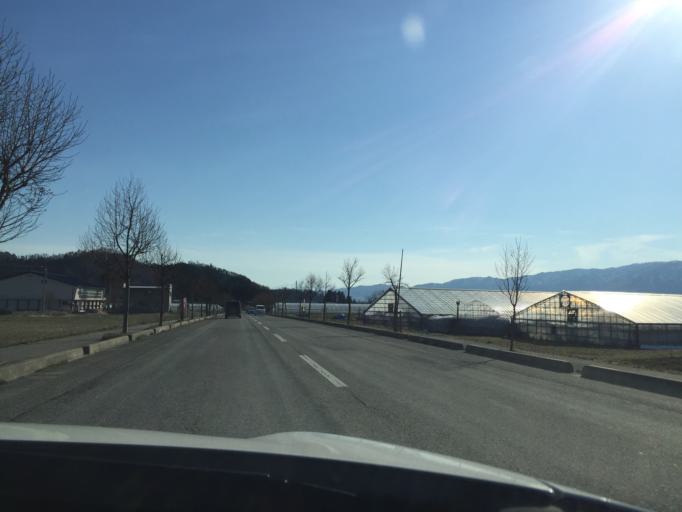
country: JP
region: Yamagata
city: Nagai
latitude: 38.1667
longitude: 140.0852
